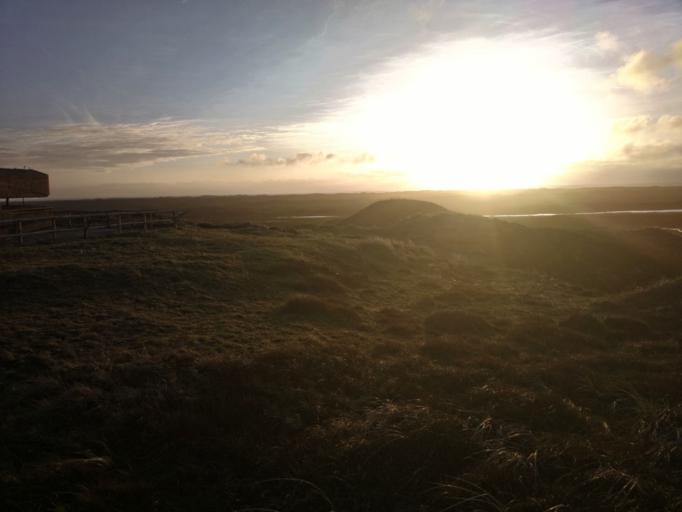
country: NL
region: North Holland
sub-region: Gemeente Den Helder
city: Den Helder
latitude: 53.0220
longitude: 4.7280
